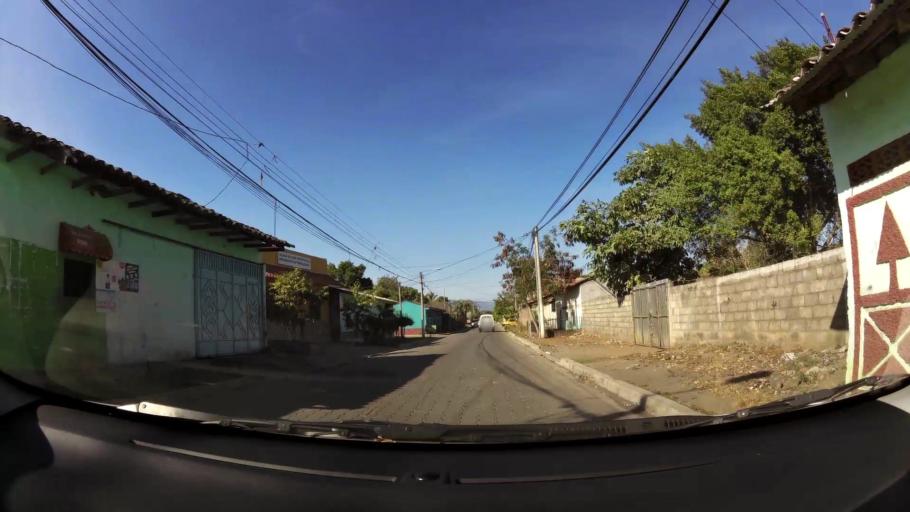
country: SV
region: San Miguel
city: San Miguel
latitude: 13.4730
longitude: -88.1938
